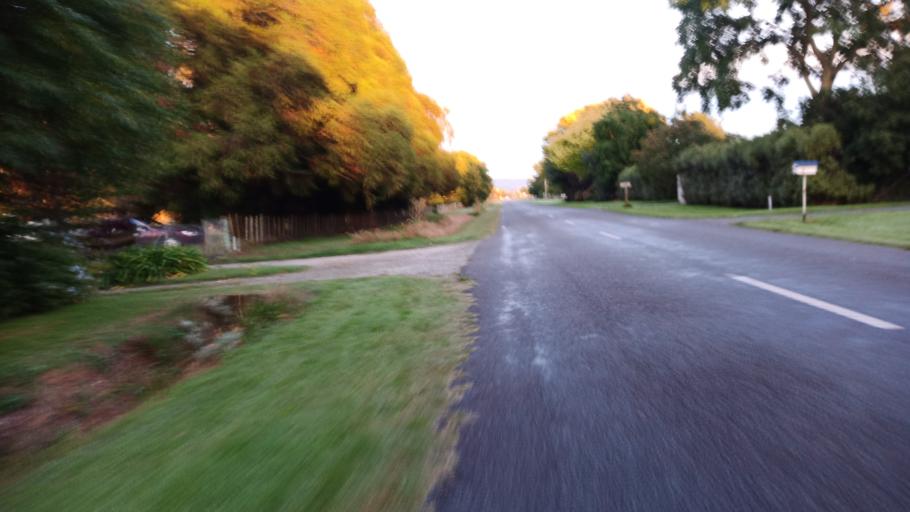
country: NZ
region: Gisborne
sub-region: Gisborne District
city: Gisborne
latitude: -38.6339
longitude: 177.9764
